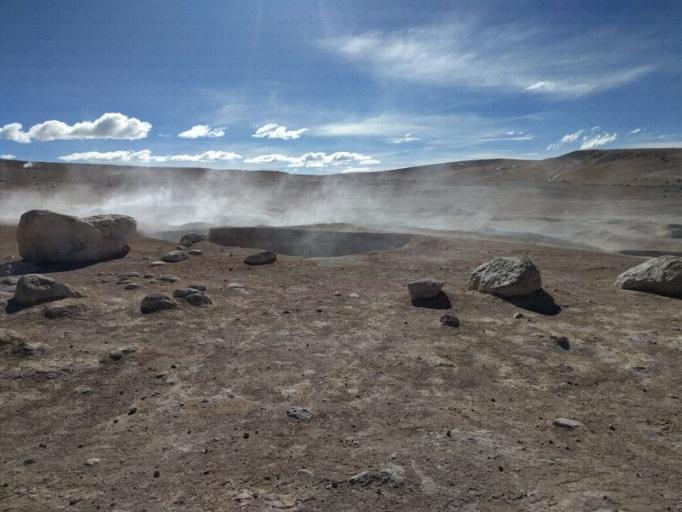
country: CL
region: Antofagasta
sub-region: Provincia de El Loa
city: San Pedro de Atacama
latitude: -22.4350
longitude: -67.7572
